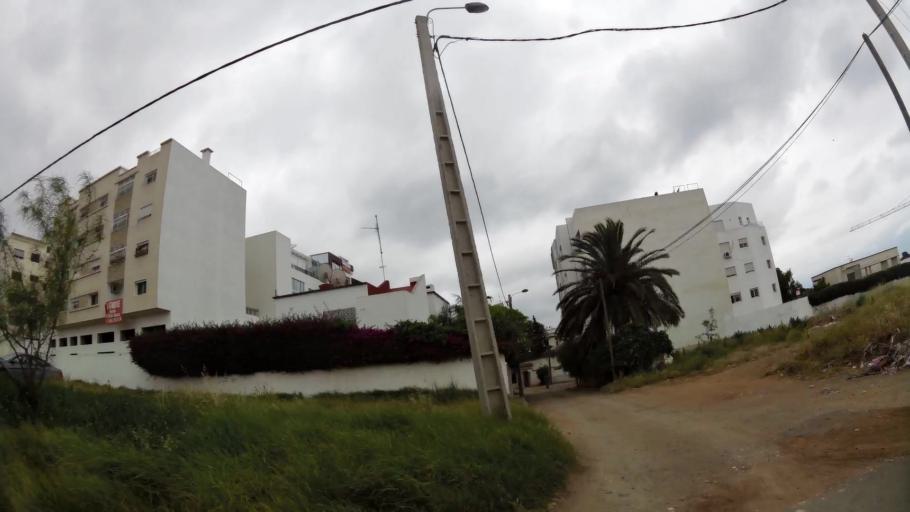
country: MA
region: Rabat-Sale-Zemmour-Zaer
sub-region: Rabat
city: Rabat
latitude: 33.9966
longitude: -6.8215
